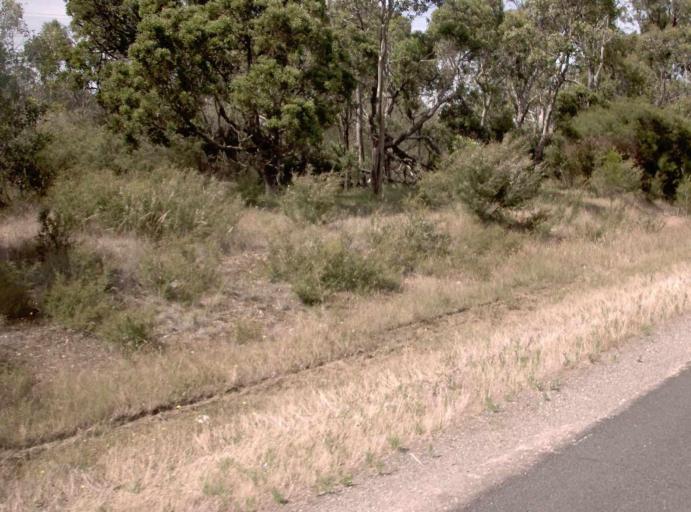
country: AU
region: Victoria
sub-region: East Gippsland
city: Bairnsdale
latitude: -37.8598
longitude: 147.5193
